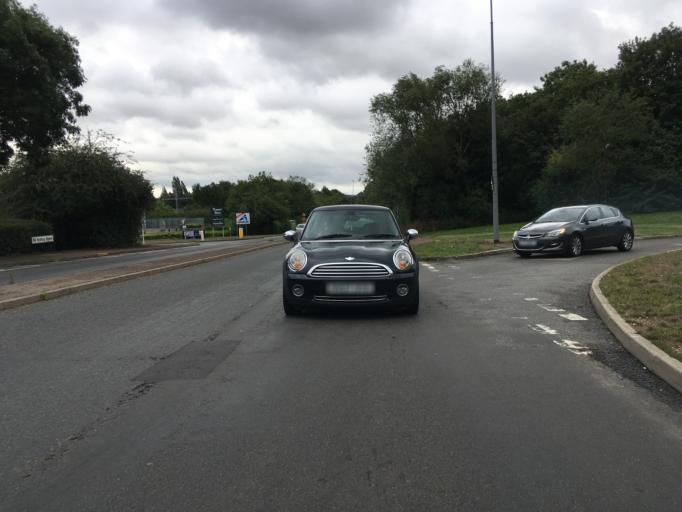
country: GB
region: England
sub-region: Buckinghamshire
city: Bletchley
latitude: 52.0114
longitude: -0.7479
